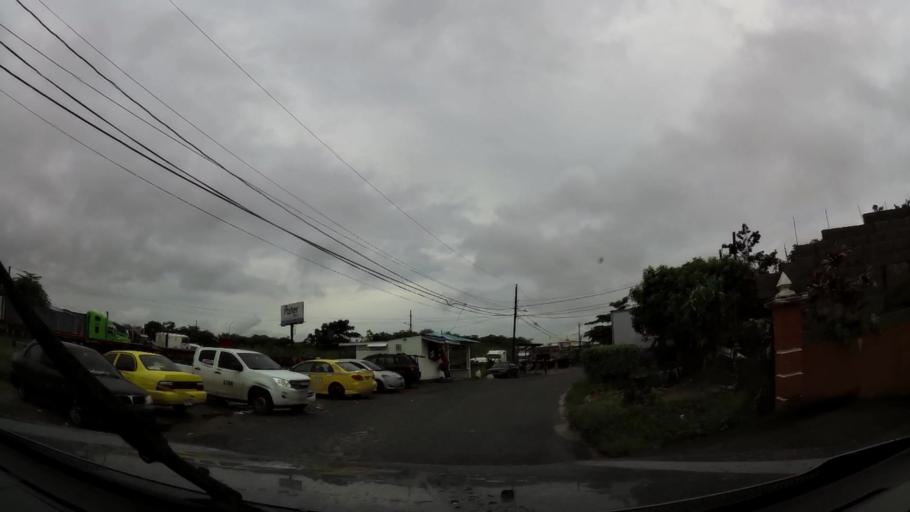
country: PA
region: Colon
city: Arco Iris
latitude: 9.3352
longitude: -79.8782
